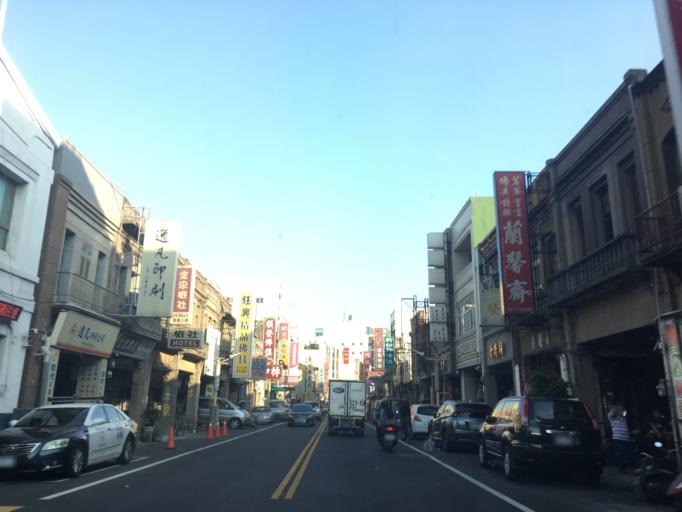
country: TW
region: Taiwan
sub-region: Changhua
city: Chang-hua
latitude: 24.0530
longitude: 120.4358
